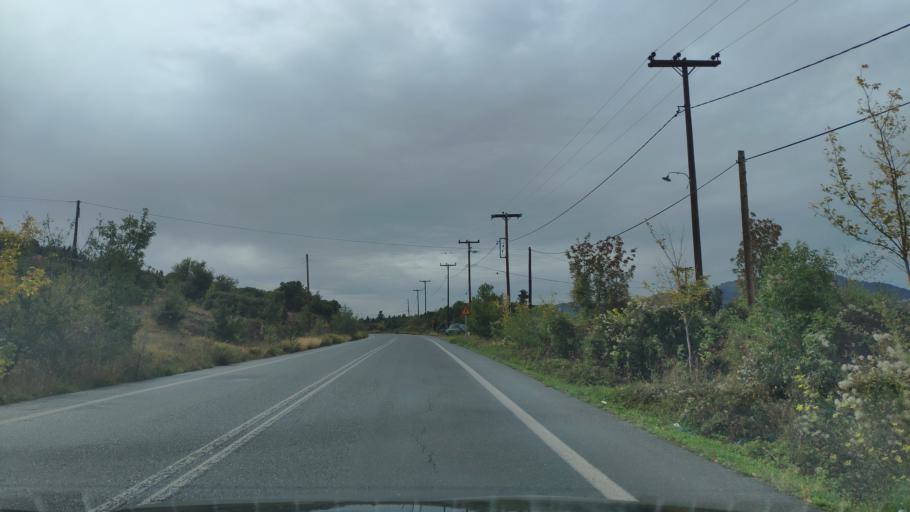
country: GR
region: Peloponnese
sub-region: Nomos Arkadias
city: Langadhia
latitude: 37.6669
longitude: 22.1936
